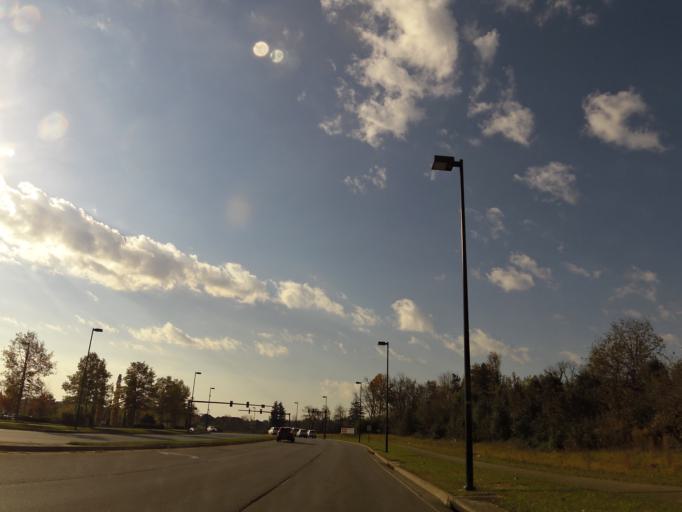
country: US
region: Kentucky
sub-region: Fayette County
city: Lexington-Fayette
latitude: 38.0409
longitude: -84.4289
